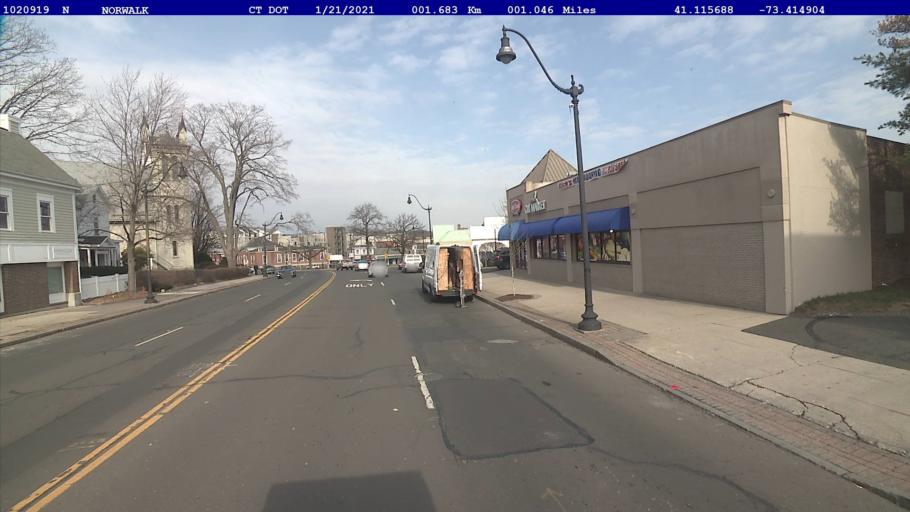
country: US
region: Connecticut
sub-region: Fairfield County
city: Norwalk
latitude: 41.1157
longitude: -73.4149
